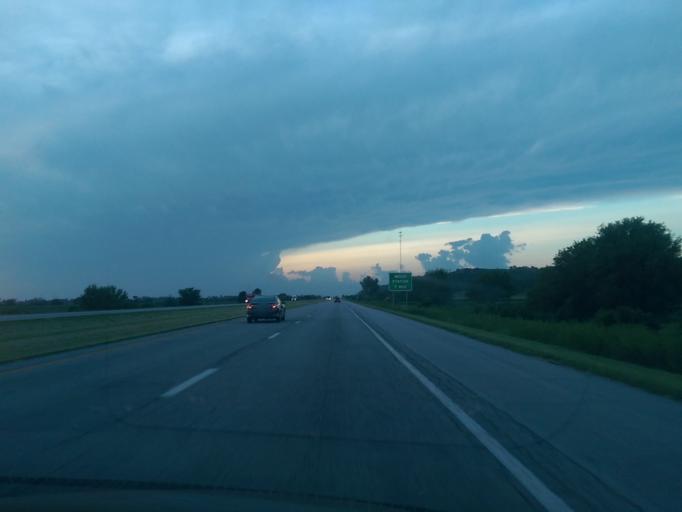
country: US
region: Iowa
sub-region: Fremont County
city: Hamburg
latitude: 40.5355
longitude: -95.6167
